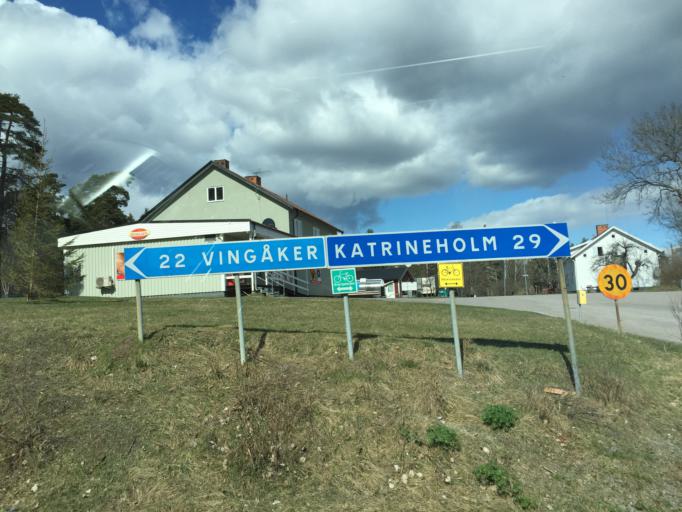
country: SE
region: Soedermanland
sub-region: Vingakers Kommun
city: Vingaker
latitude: 58.9148
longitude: 15.8680
